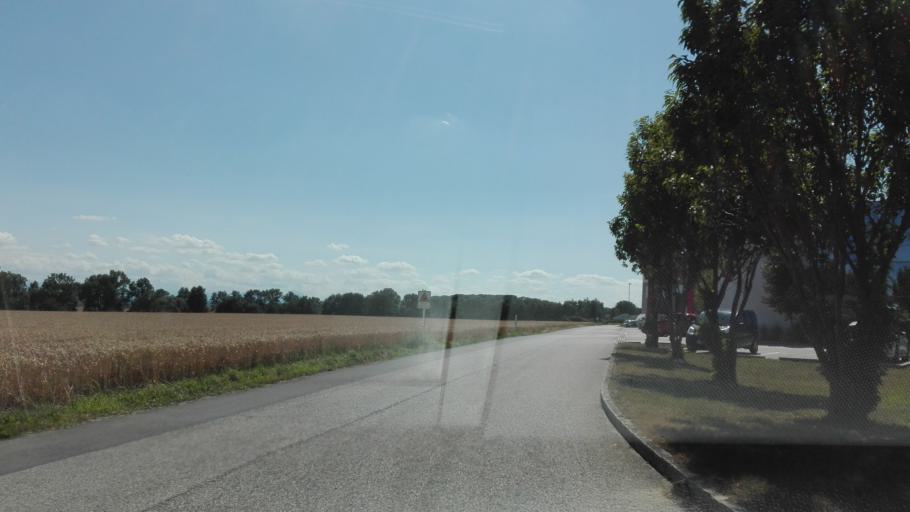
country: AT
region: Upper Austria
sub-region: Politischer Bezirk Linz-Land
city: Horsching
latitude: 48.2264
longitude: 14.1621
